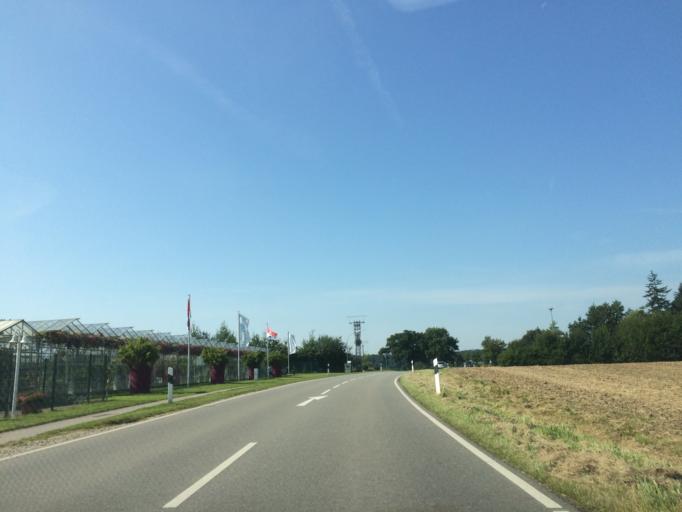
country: DE
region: Schleswig-Holstein
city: Kirchbarkau
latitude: 54.2216
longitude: 10.1407
